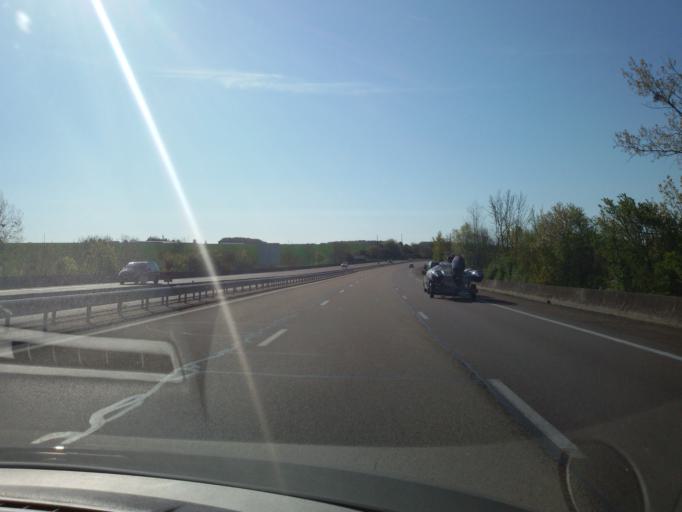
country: FR
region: Bourgogne
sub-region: Departement de l'Yonne
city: Saint-Julien-du-Sault
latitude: 47.9483
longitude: 3.2345
